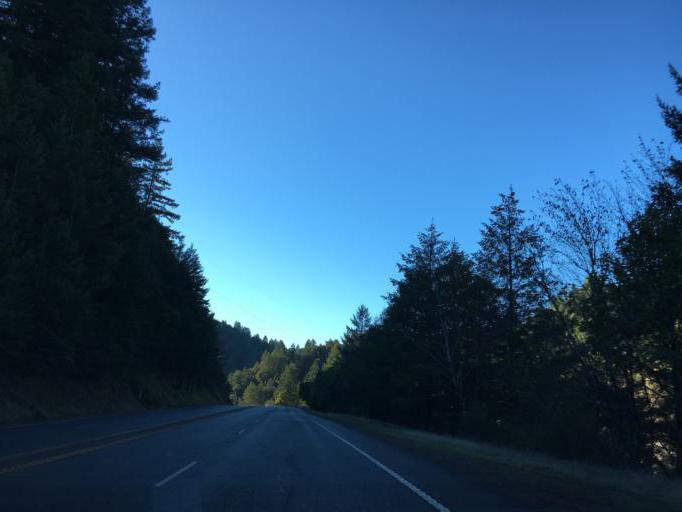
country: US
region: California
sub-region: Mendocino County
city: Laytonville
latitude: 39.8293
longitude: -123.6005
